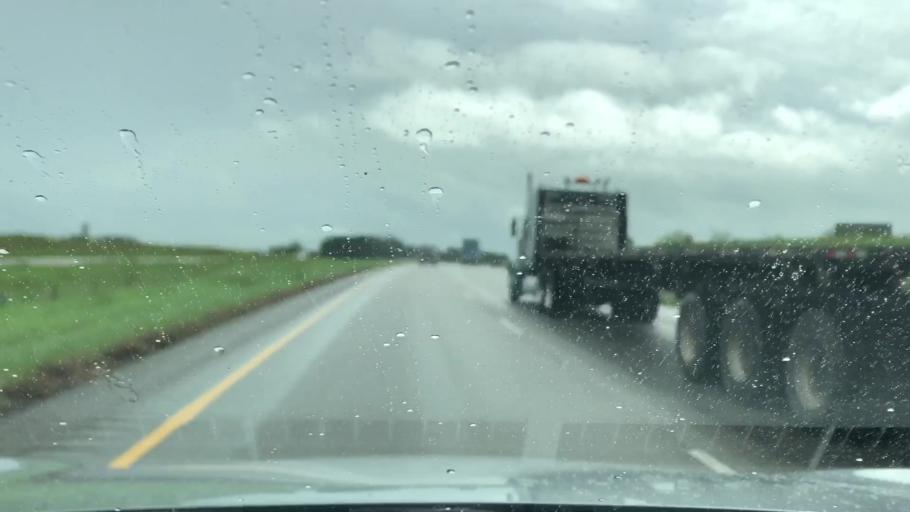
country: US
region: Texas
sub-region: Fayette County
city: Schulenburg
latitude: 29.6964
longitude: -96.8571
